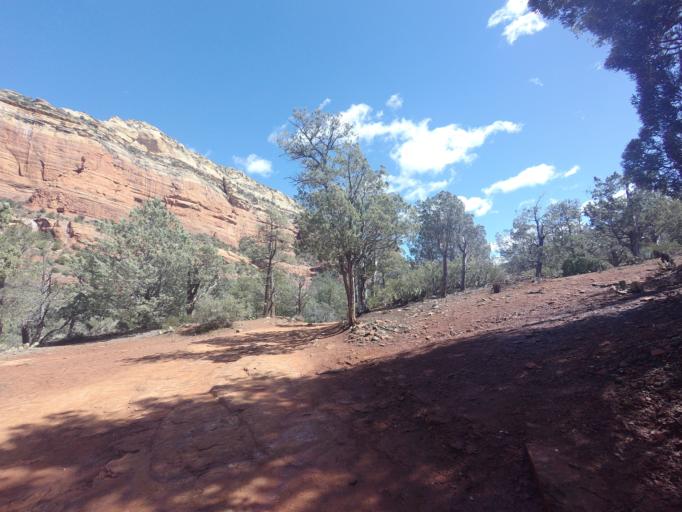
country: US
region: Arizona
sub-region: Yavapai County
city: West Sedona
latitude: 34.9011
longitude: -111.8087
